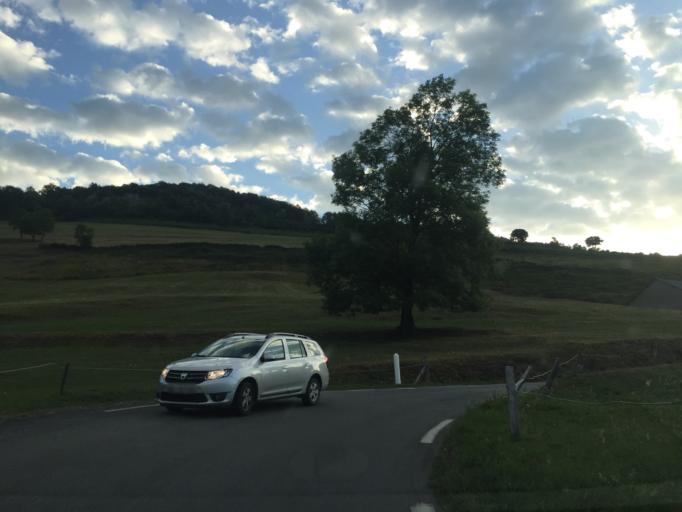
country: FR
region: Midi-Pyrenees
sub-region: Departement des Hautes-Pyrenees
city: Saint-Lary-Soulan
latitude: 42.9281
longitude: 0.3451
